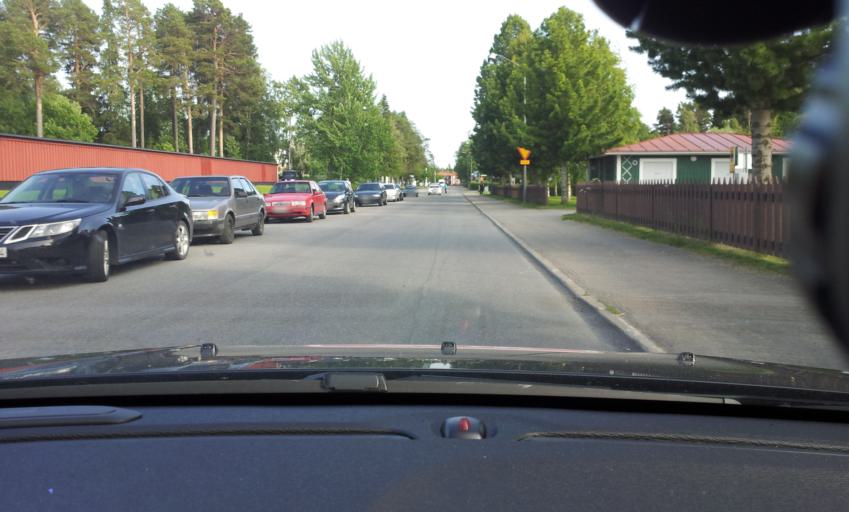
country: SE
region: Jaemtland
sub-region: OEstersunds Kommun
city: Ostersund
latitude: 63.1684
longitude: 14.6618
